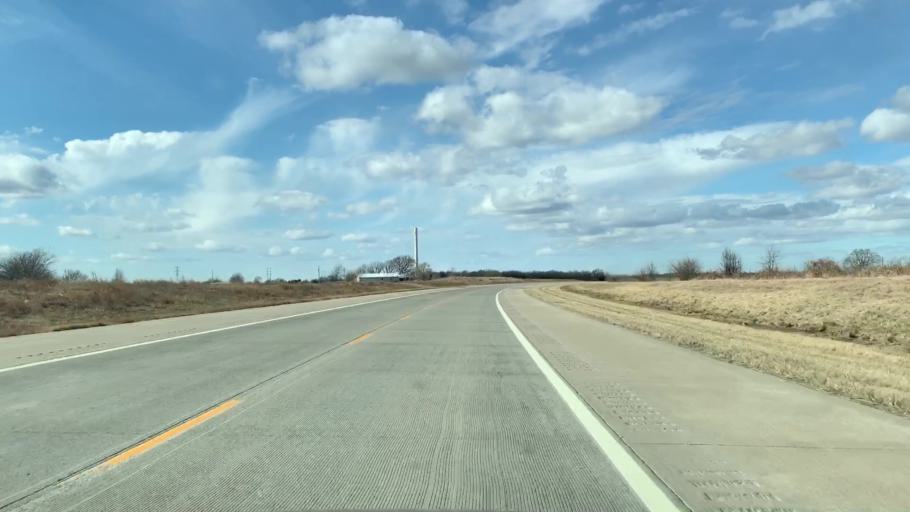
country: US
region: Kansas
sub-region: Labette County
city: Parsons
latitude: 37.3521
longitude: -95.2078
